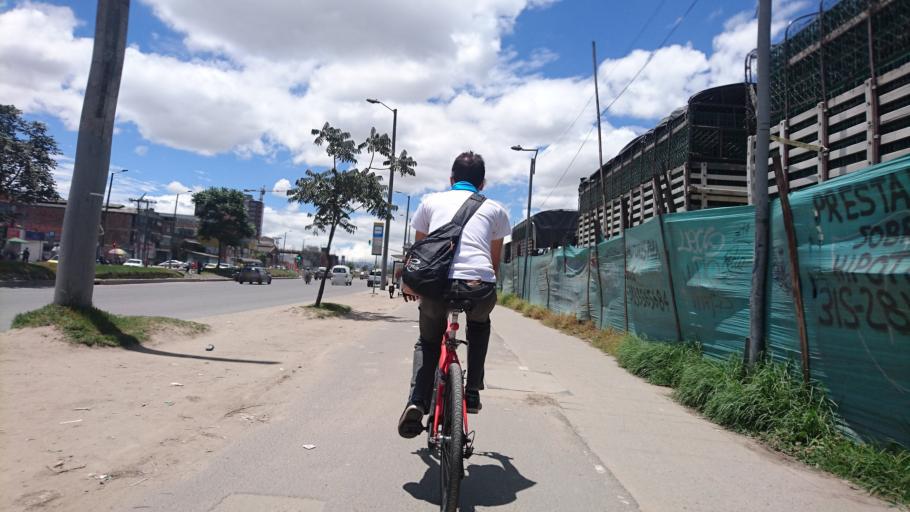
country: CO
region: Bogota D.C.
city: Bogota
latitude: 4.6573
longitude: -74.1382
